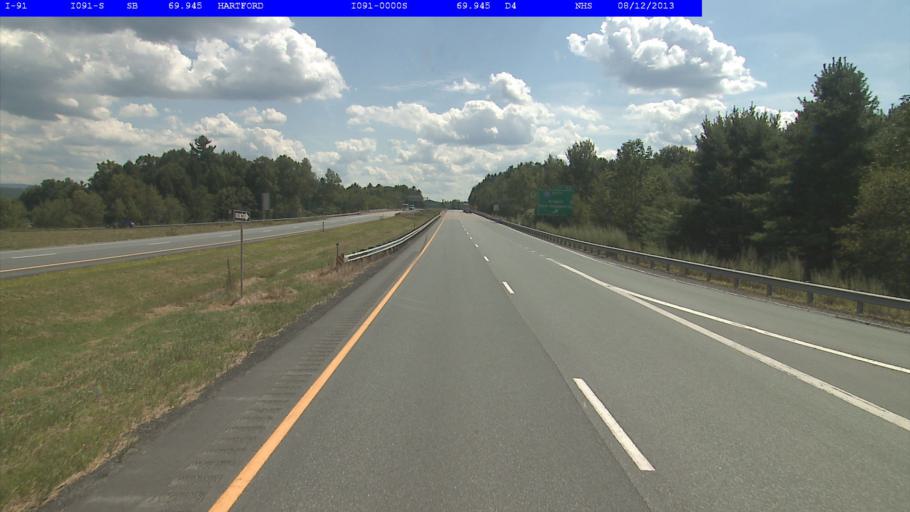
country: US
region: Vermont
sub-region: Windsor County
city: White River Junction
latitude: 43.6419
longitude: -72.3385
